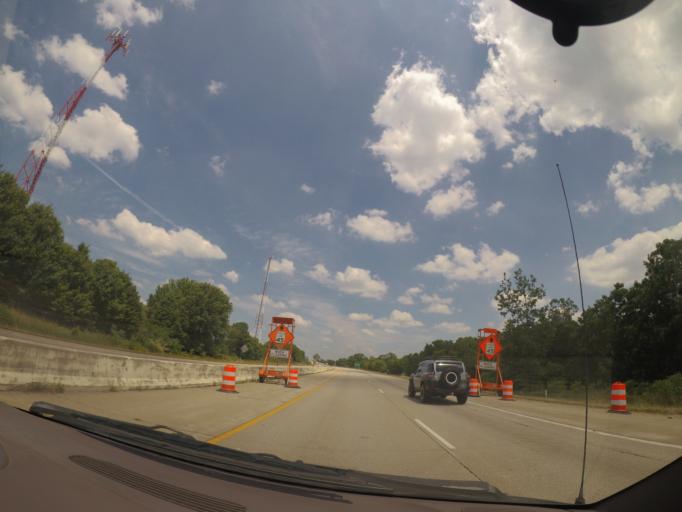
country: US
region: Indiana
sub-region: Saint Joseph County
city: Osceola
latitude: 41.6192
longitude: -86.0407
